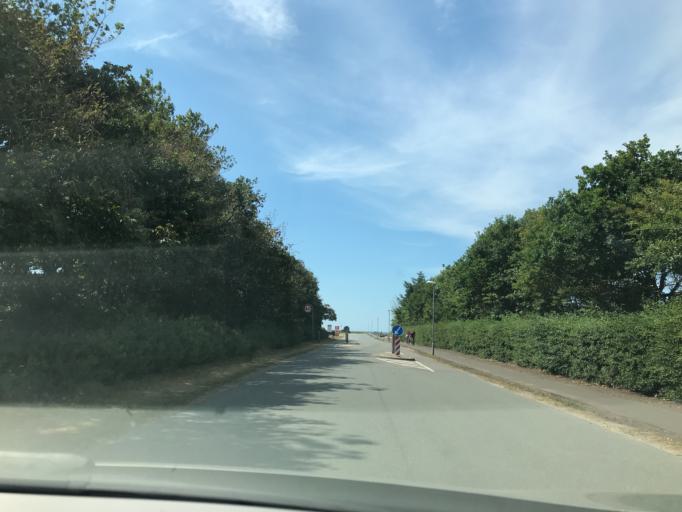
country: DK
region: Central Jutland
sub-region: Ringkobing-Skjern Kommune
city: Skjern
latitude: 55.8923
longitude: 8.3646
